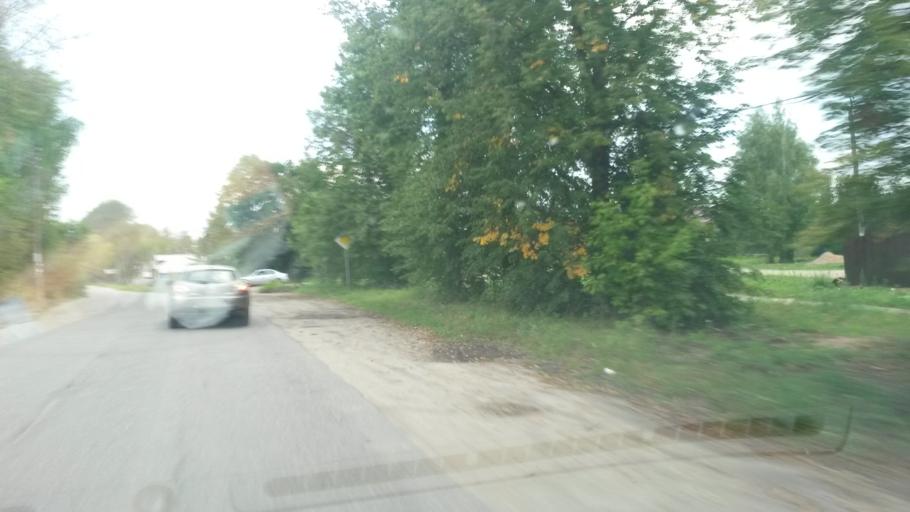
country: RU
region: Jaroslavl
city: Petrovsk
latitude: 57.0056
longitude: 39.2720
